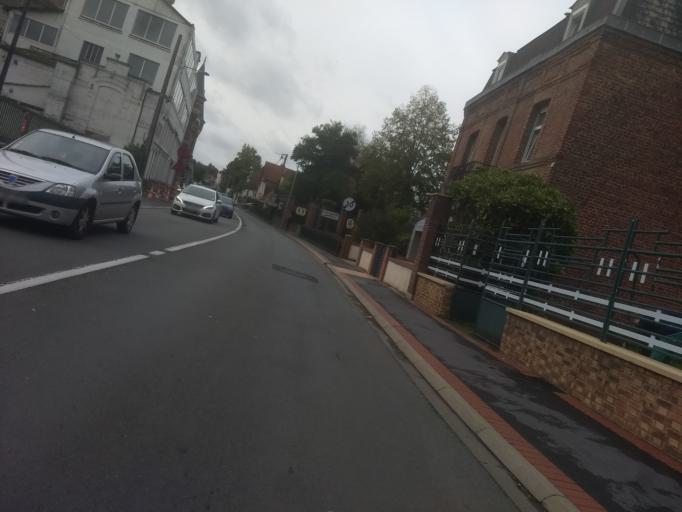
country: FR
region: Nord-Pas-de-Calais
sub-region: Departement du Pas-de-Calais
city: Saint-Nicolas
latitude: 50.2999
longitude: 2.7739
